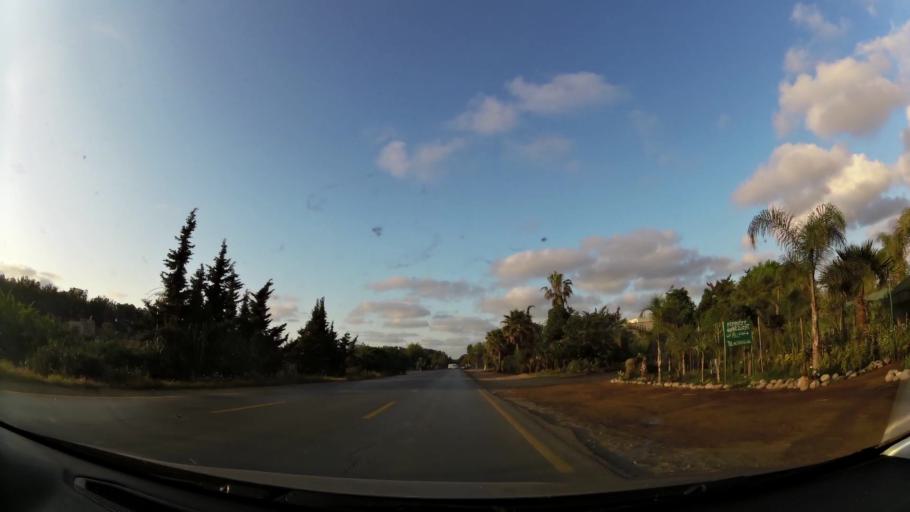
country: MA
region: Gharb-Chrarda-Beni Hssen
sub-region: Kenitra Province
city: Kenitra
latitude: 34.2093
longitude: -6.6717
